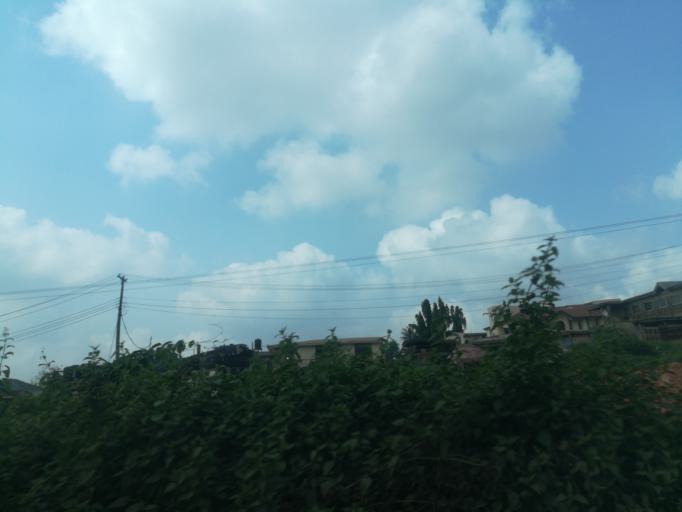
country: NG
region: Oyo
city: Ibadan
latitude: 7.4218
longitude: 3.9379
